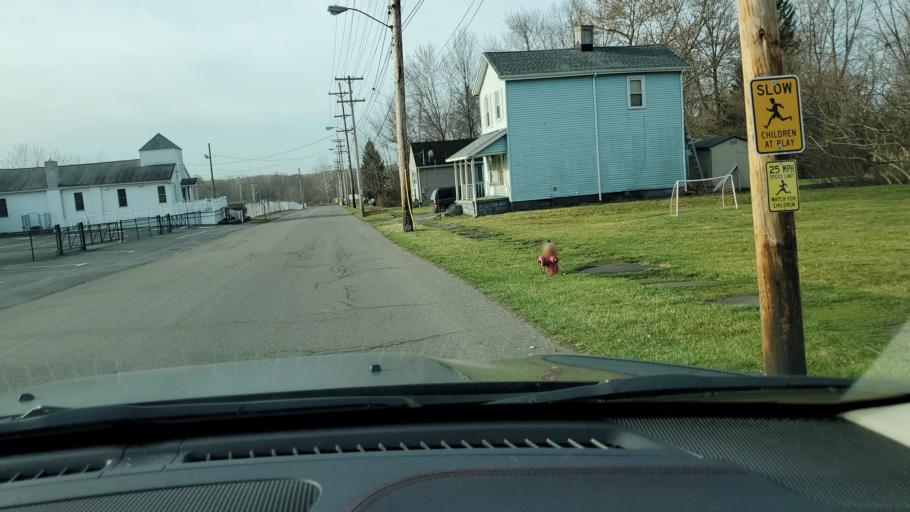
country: US
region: Ohio
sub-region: Trumbull County
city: Niles
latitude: 41.1783
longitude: -80.7546
